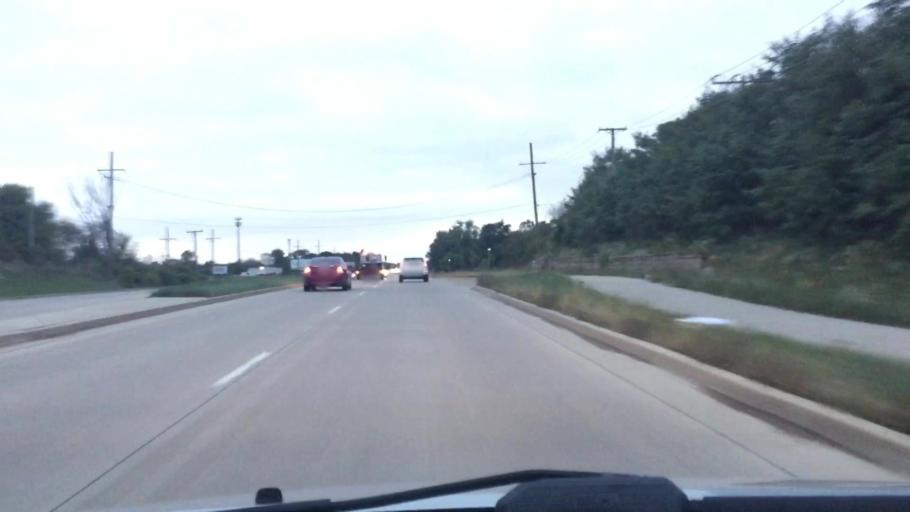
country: US
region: Illinois
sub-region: McHenry County
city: Algonquin
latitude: 42.2008
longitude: -88.2864
